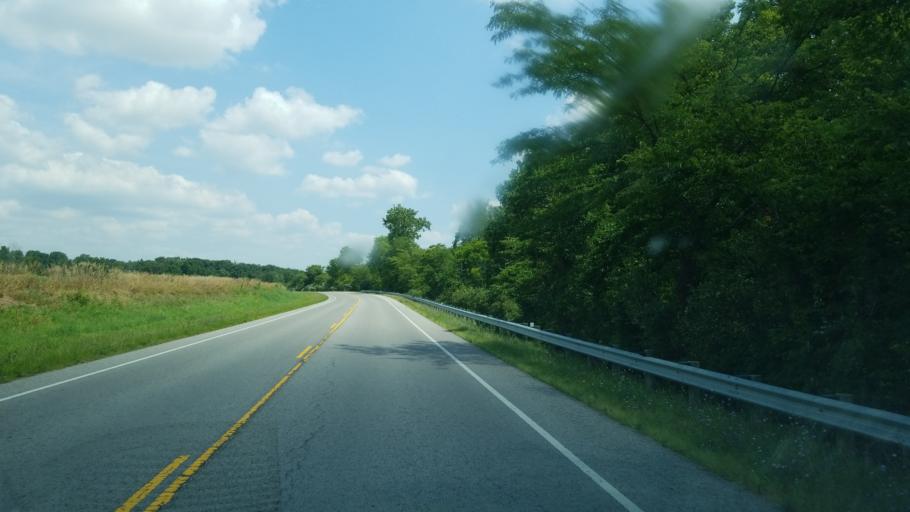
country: US
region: Ohio
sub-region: Henry County
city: Holgate
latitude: 41.3053
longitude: -84.2244
